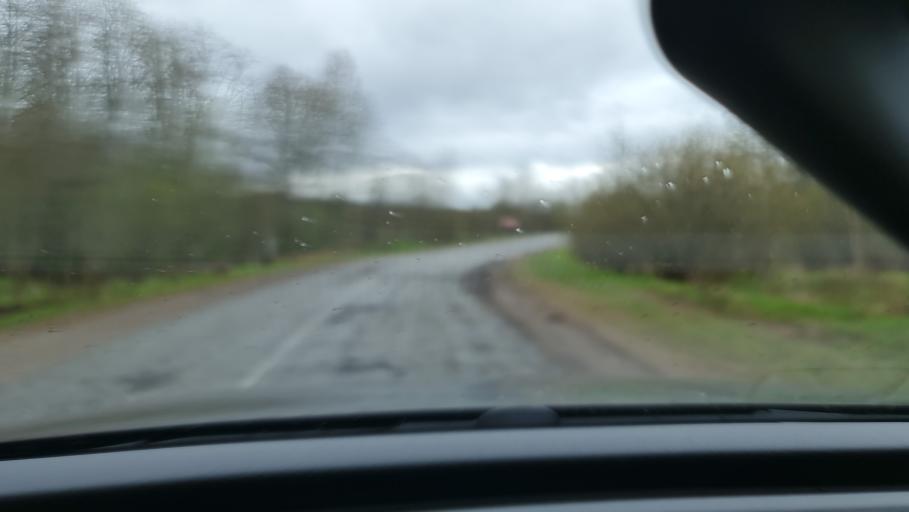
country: RU
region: Novgorod
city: Marevo
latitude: 57.2454
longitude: 32.0625
